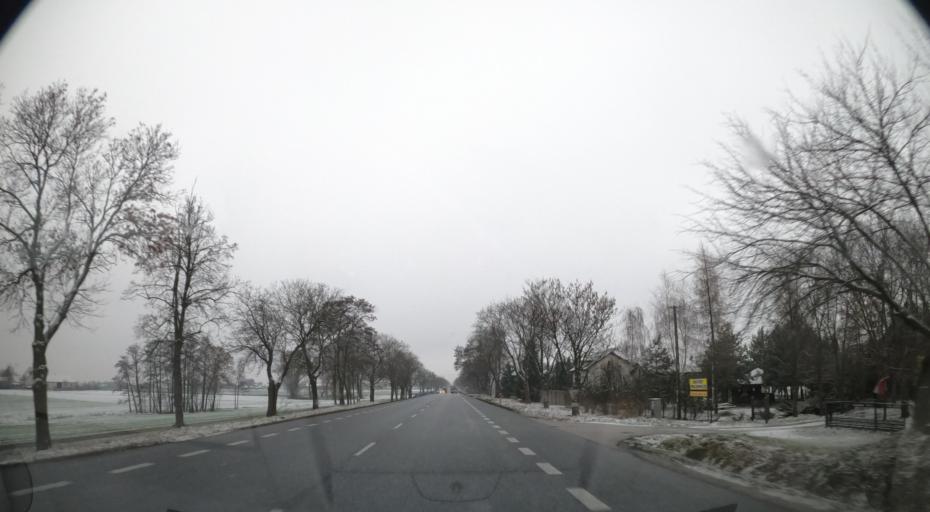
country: PL
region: Masovian Voivodeship
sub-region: Powiat warszawski zachodni
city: Bieniewice
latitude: 52.2018
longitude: 20.5409
